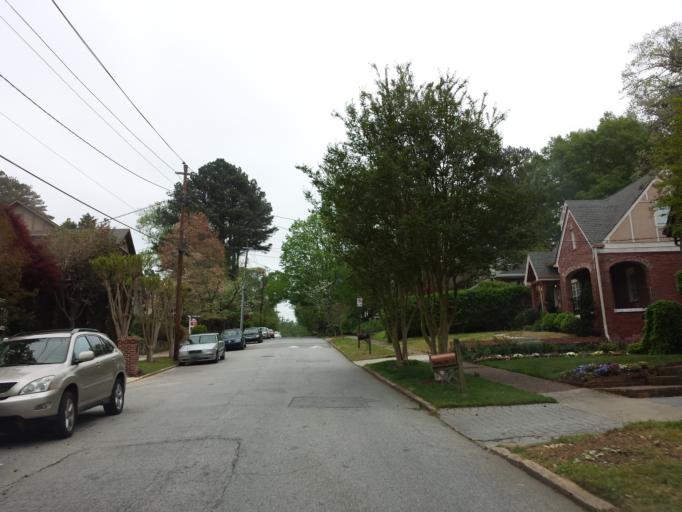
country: US
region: Georgia
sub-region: DeKalb County
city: Druid Hills
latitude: 33.7952
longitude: -84.3628
